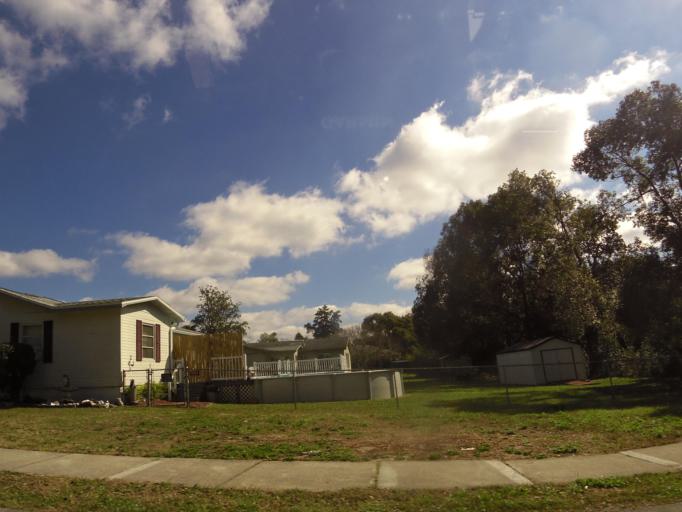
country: US
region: Florida
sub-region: Volusia County
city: Orange City
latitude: 28.9461
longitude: -81.3072
